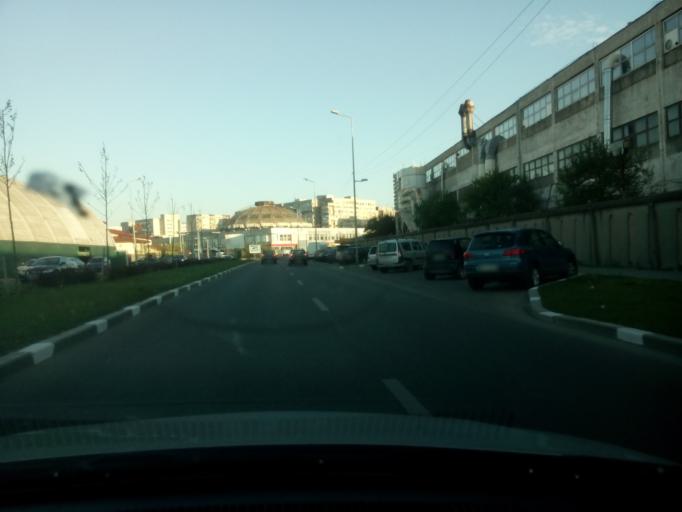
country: RO
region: Ilfov
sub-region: Comuna Fundeni-Dobroesti
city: Fundeni
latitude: 44.4465
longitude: 26.1553
